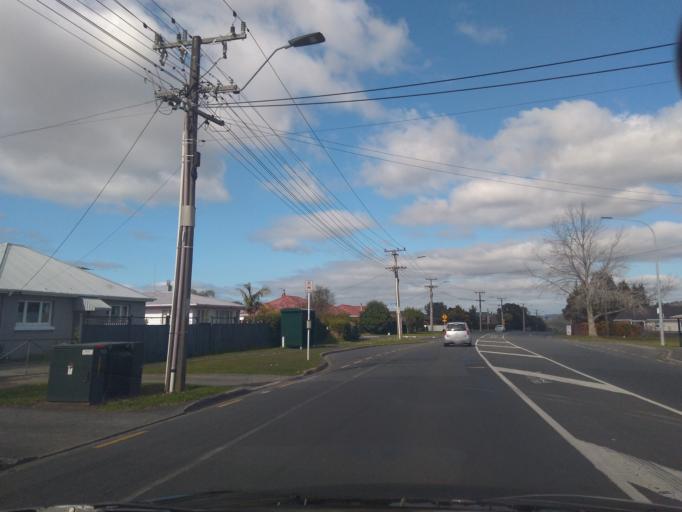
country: NZ
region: Northland
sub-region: Whangarei
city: Whangarei
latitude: -35.6921
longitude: 174.3271
